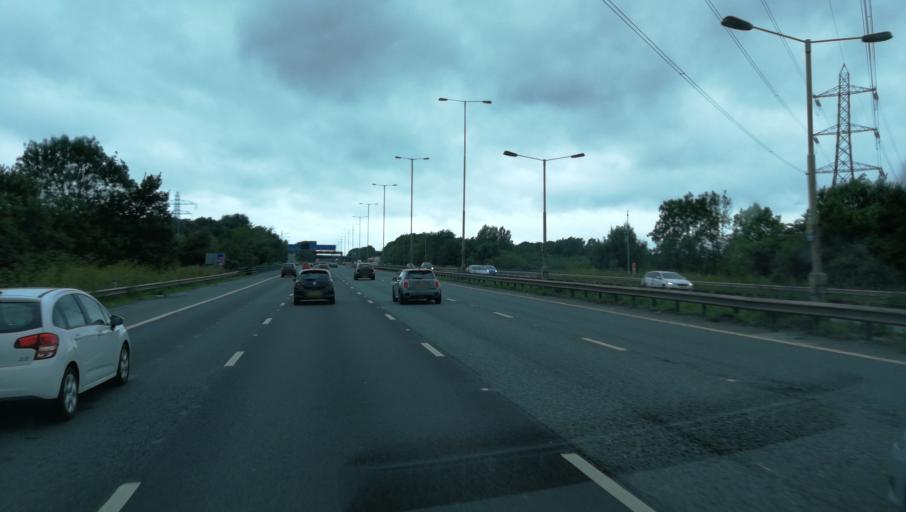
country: GB
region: England
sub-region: Borough of Bury
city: Whitefield
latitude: 53.5288
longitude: -2.3246
